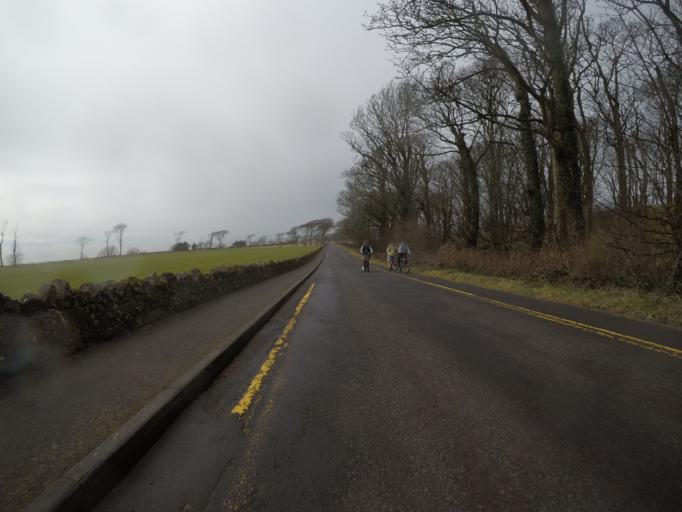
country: GB
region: Scotland
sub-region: North Ayrshire
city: West Kilbride
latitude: 55.6960
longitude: -4.8773
